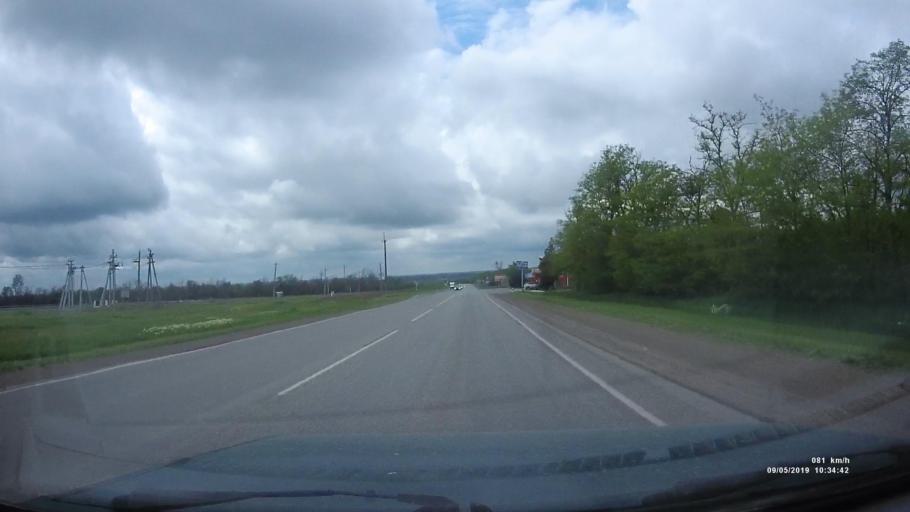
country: RU
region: Rostov
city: Peshkovo
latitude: 47.0511
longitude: 39.4175
